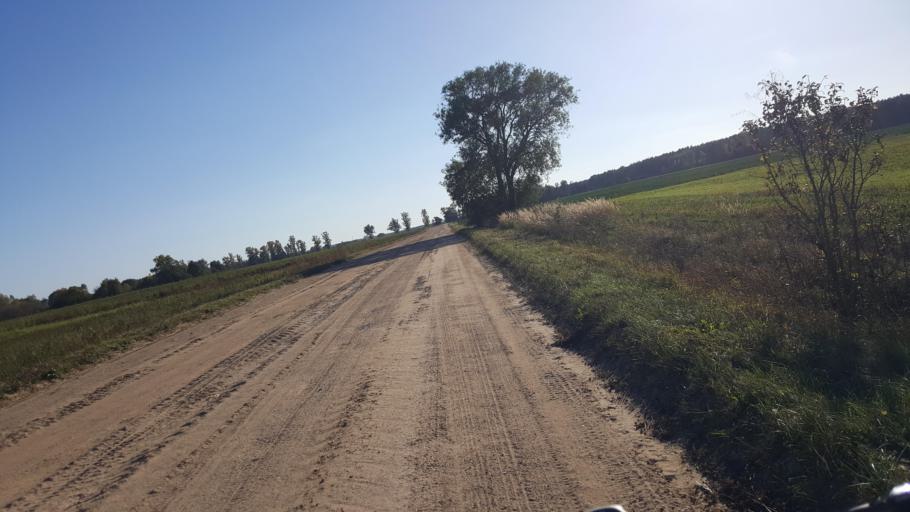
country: BY
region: Brest
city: Kamyanyets
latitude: 52.3812
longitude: 23.8815
